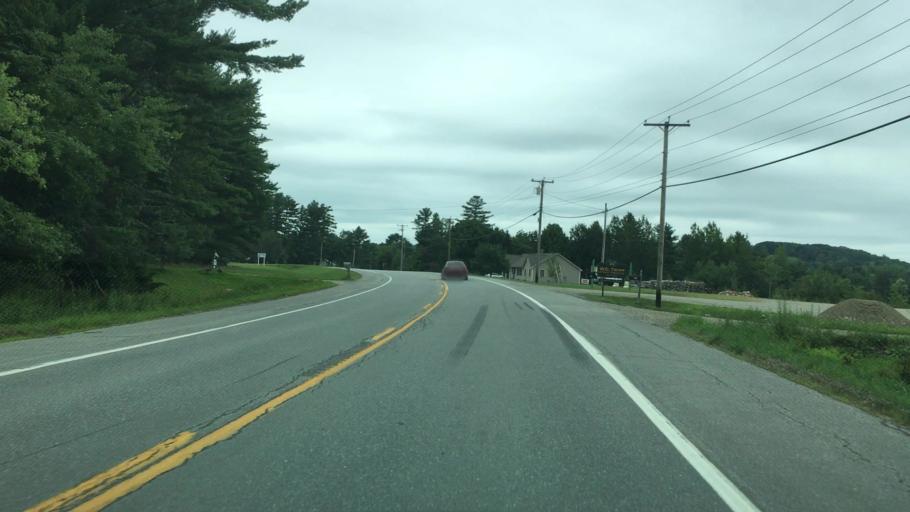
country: US
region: Maine
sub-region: Waldo County
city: Frankfort
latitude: 44.6183
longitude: -68.8698
